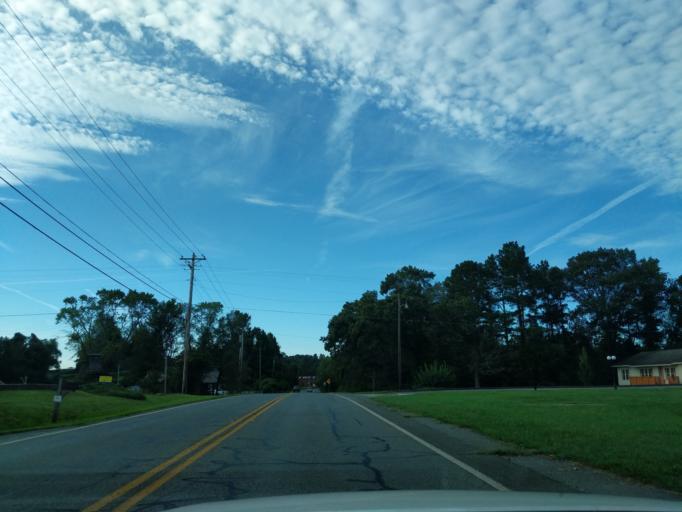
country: US
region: Georgia
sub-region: Fannin County
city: McCaysville
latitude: 34.9694
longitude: -84.3704
